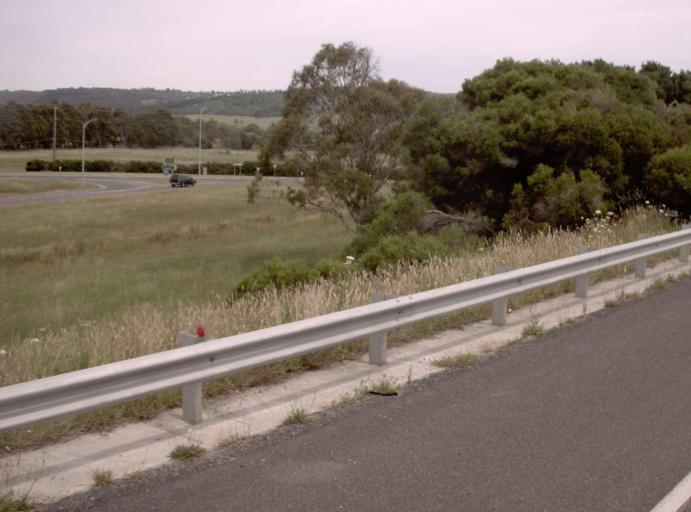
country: AU
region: Victoria
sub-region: Mornington Peninsula
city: Safety Beach
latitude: -38.3288
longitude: 144.9912
